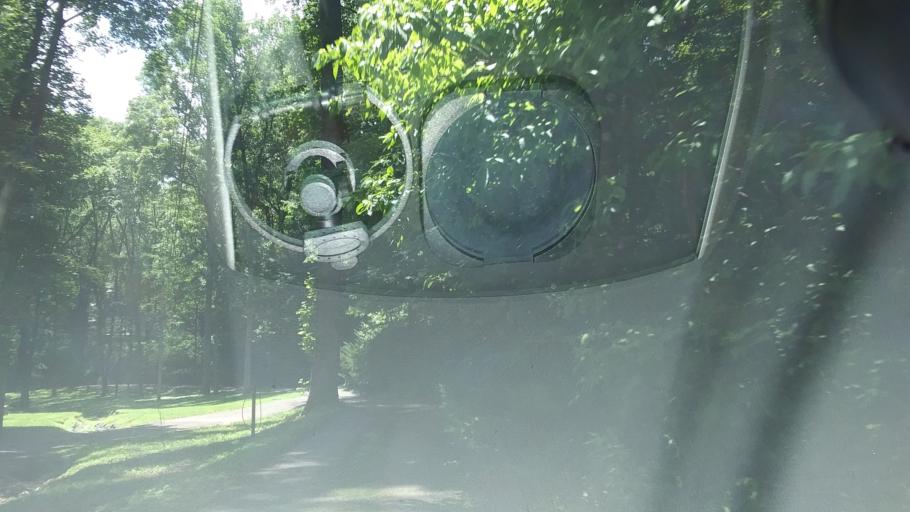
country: US
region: Tennessee
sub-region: Davidson County
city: Belle Meade
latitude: 36.0918
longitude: -86.9519
